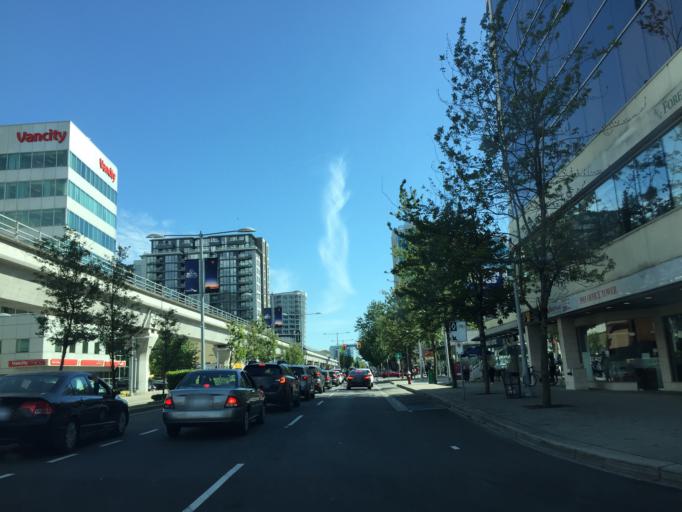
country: CA
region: British Columbia
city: Richmond
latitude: 49.1712
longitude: -123.1367
